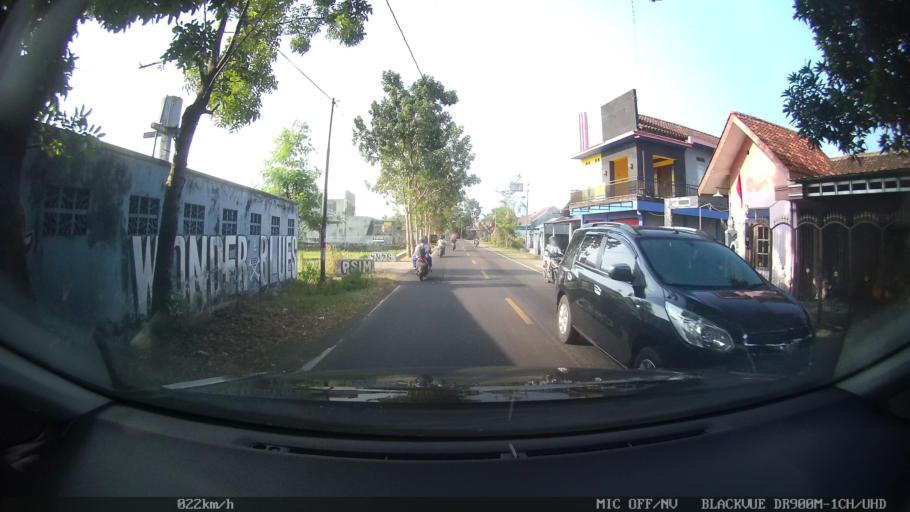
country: ID
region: Daerah Istimewa Yogyakarta
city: Bantul
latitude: -7.8850
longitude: 110.3183
